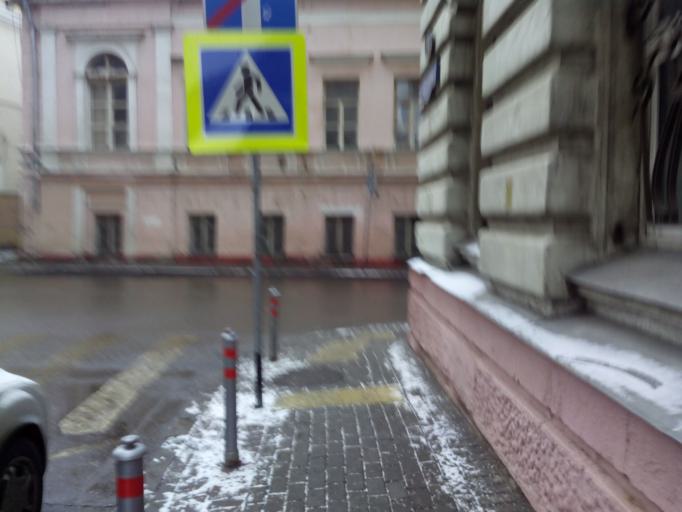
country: RU
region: Moscow
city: Moscow
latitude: 55.7655
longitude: 37.6327
